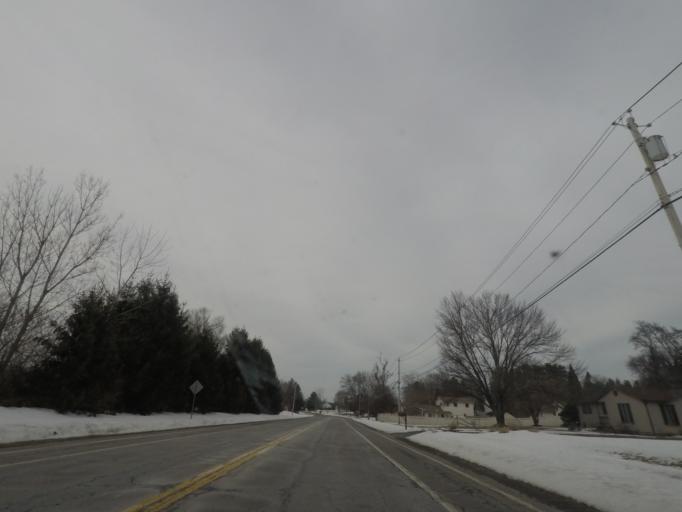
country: US
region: New York
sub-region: Albany County
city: Westmere
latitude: 42.6763
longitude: -73.8935
